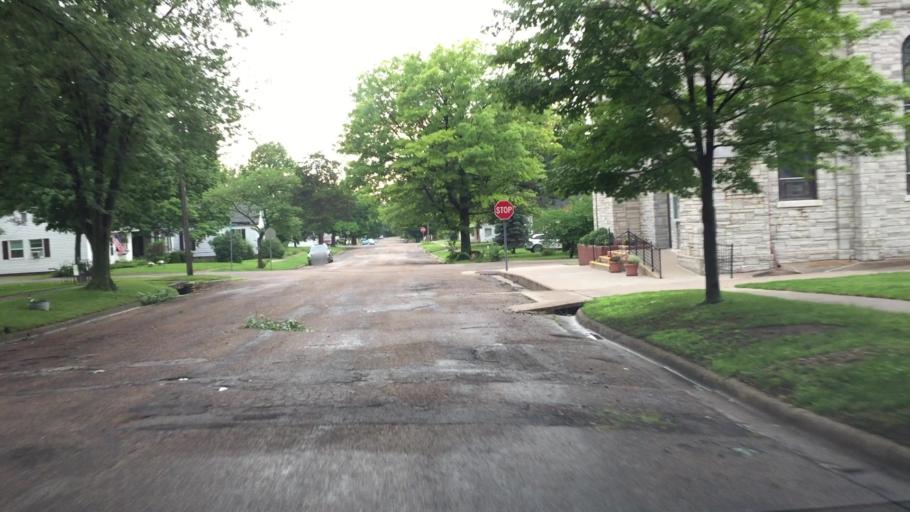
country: US
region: Illinois
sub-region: Hancock County
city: Warsaw
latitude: 40.3567
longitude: -91.4324
